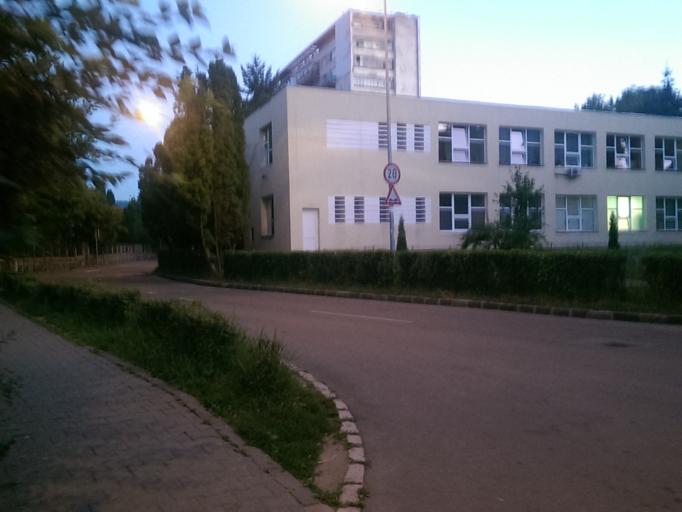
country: RO
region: Cluj
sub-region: Municipiul Cluj-Napoca
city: Cluj-Napoca
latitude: 46.7666
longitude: 23.6244
